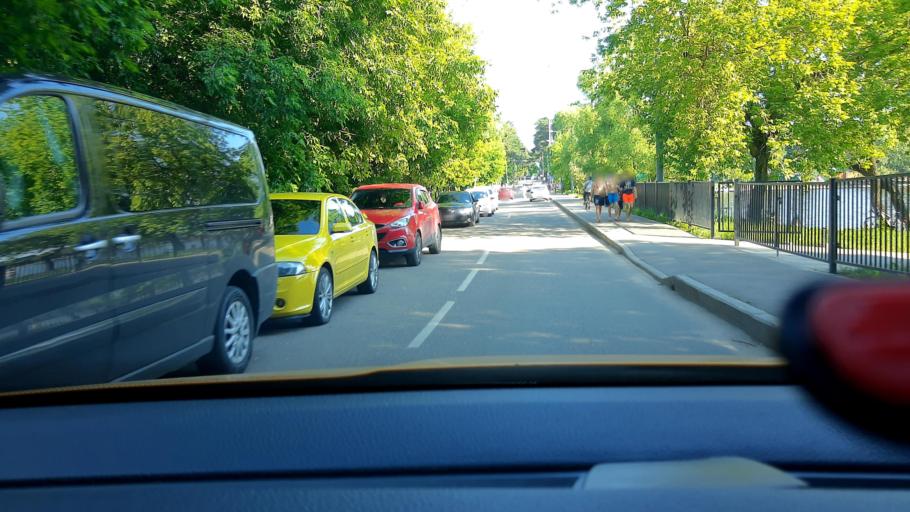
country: RU
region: Moskovskaya
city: Zarech'ye
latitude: 55.6755
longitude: 37.4101
